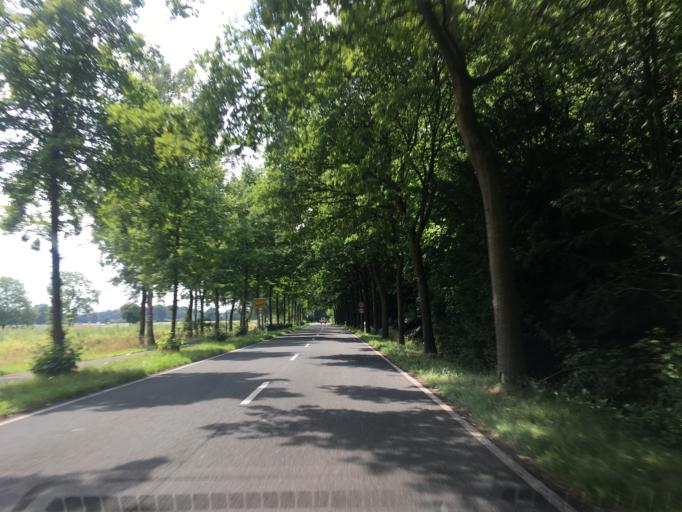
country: DE
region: North Rhine-Westphalia
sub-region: Regierungsbezirk Munster
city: Senden
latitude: 51.8507
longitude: 7.4691
